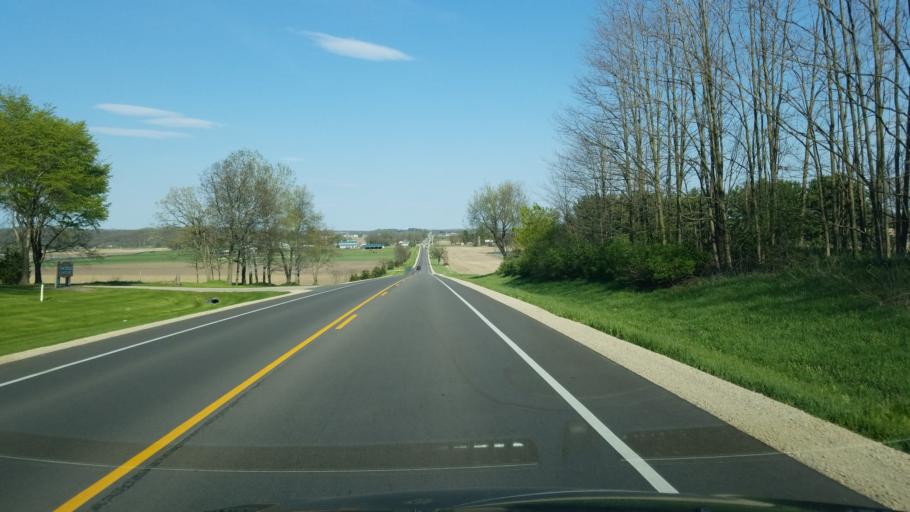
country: US
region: Wisconsin
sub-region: Dane County
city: Fitchburg
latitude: 42.9504
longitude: -89.4515
